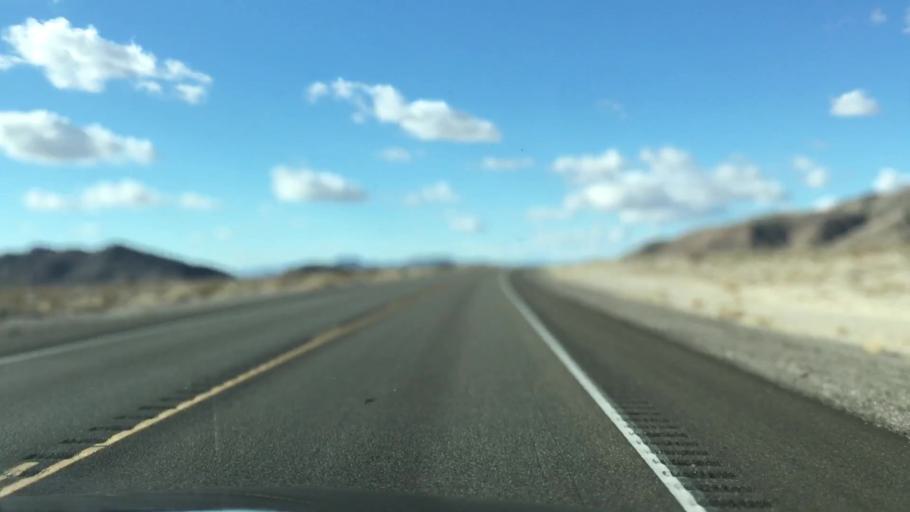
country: US
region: Nevada
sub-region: Nye County
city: Pahrump
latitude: 36.5750
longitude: -116.1879
